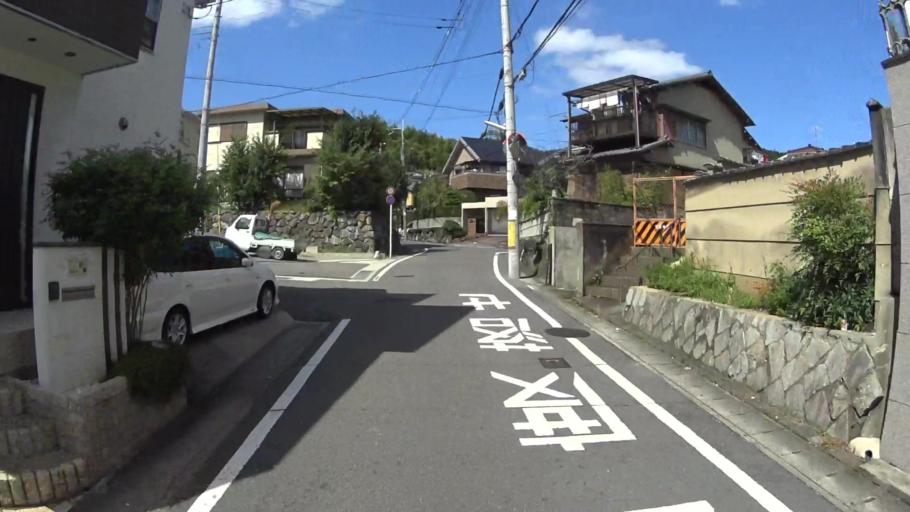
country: JP
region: Kyoto
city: Uji
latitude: 34.9369
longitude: 135.7909
